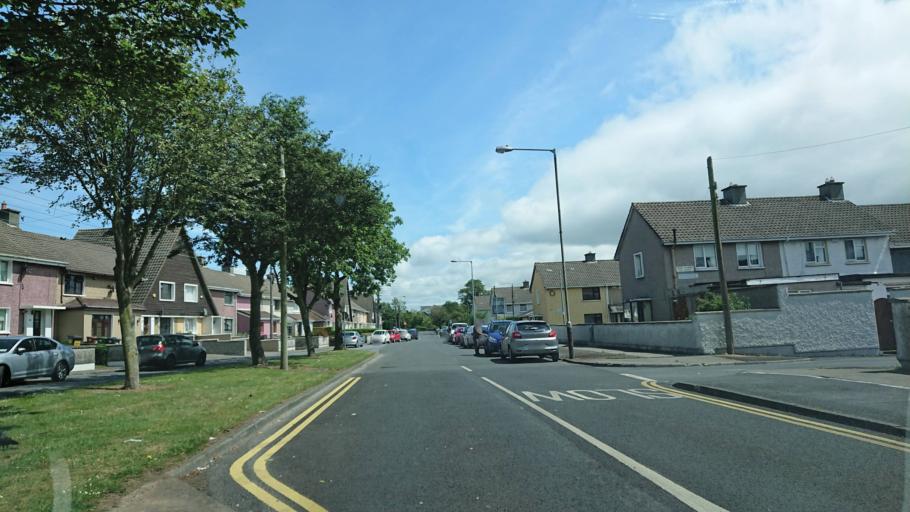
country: IE
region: Munster
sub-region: Waterford
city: Waterford
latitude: 52.2527
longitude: -7.1324
